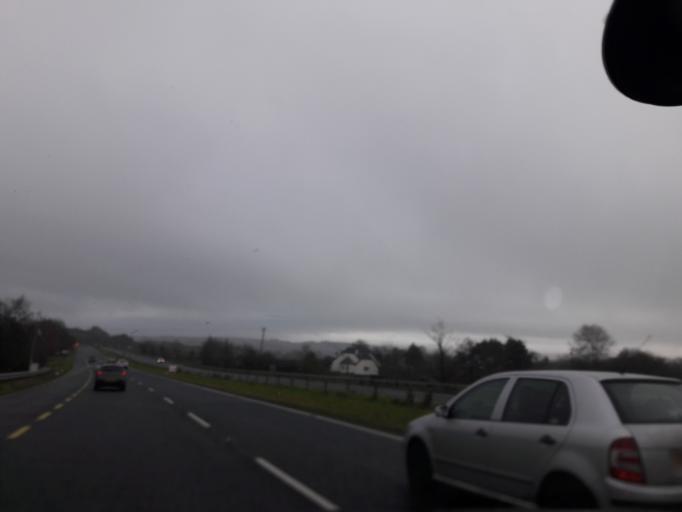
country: IE
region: Ulster
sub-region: County Donegal
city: Raphoe
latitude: 54.9468
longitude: -7.6465
